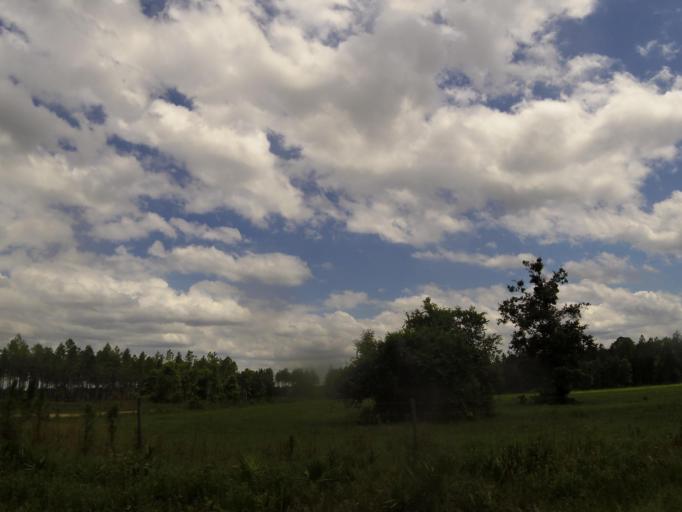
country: US
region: Florida
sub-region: Clay County
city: Asbury Lake
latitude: 29.9014
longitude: -81.8269
